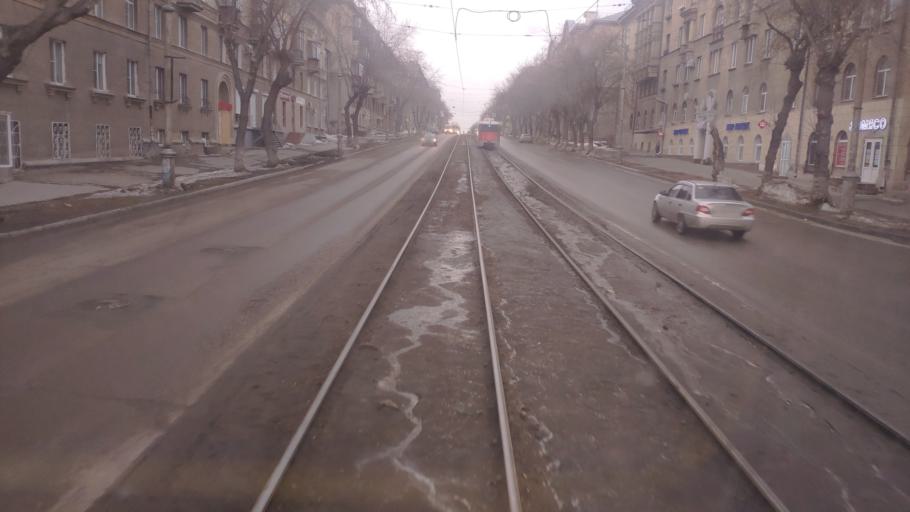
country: RU
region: Chelyabinsk
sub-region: Gorod Magnitogorsk
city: Magnitogorsk
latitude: 53.4208
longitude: 59.0002
